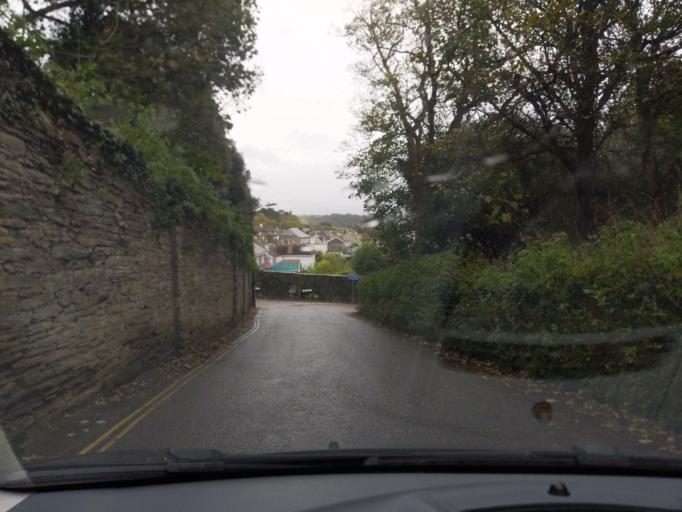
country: GB
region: England
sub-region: Cornwall
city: Padstow
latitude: 50.5413
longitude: -4.9453
